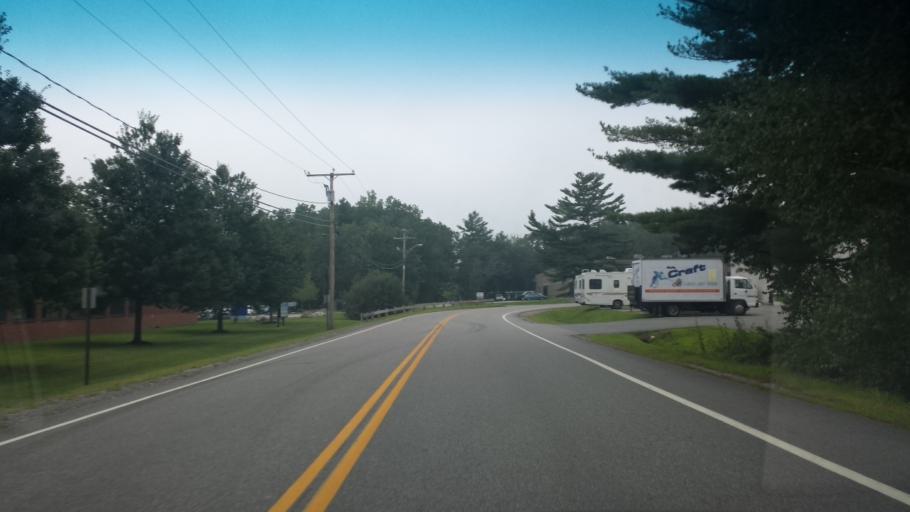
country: US
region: Maine
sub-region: Cumberland County
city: South Portland Gardens
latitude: 43.6297
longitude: -70.3258
